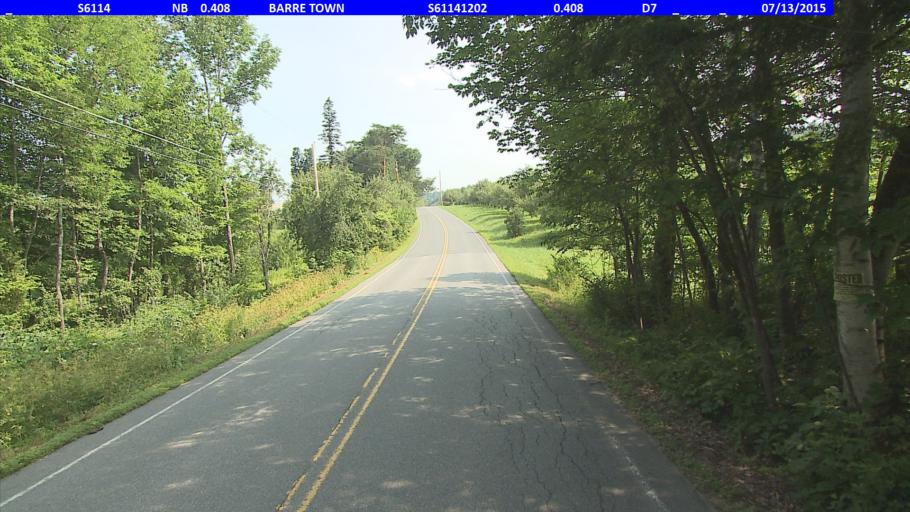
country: US
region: Vermont
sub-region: Washington County
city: Barre
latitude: 44.1973
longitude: -72.4782
